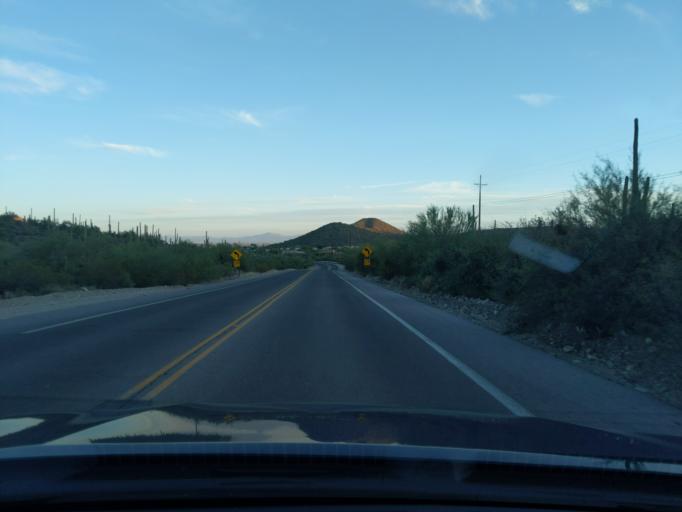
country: US
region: Arizona
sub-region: Pima County
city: Tucson Estates
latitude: 32.2276
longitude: -111.0394
